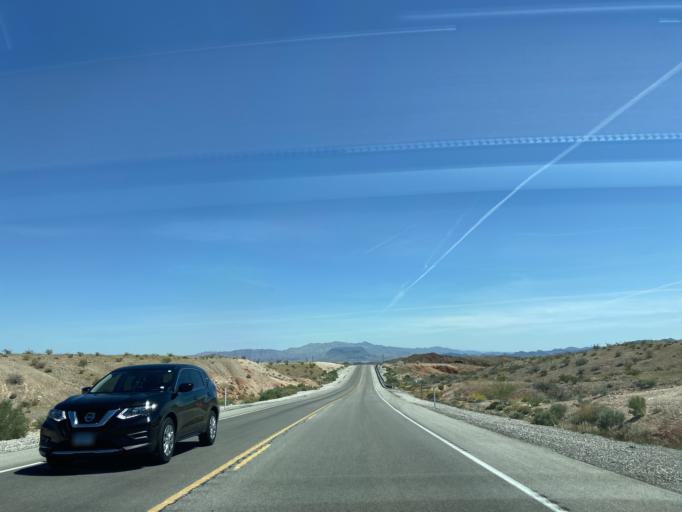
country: US
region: Nevada
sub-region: Clark County
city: Nellis Air Force Base
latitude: 36.2014
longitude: -114.9366
